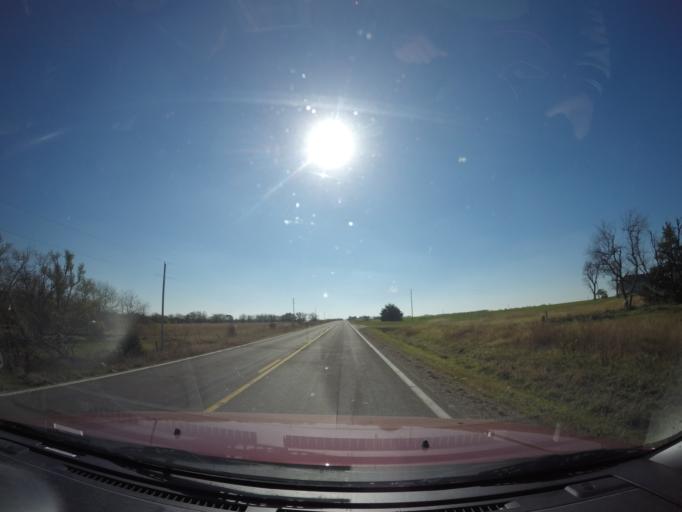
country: US
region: Kansas
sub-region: Morris County
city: Council Grove
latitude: 38.8213
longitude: -96.5014
